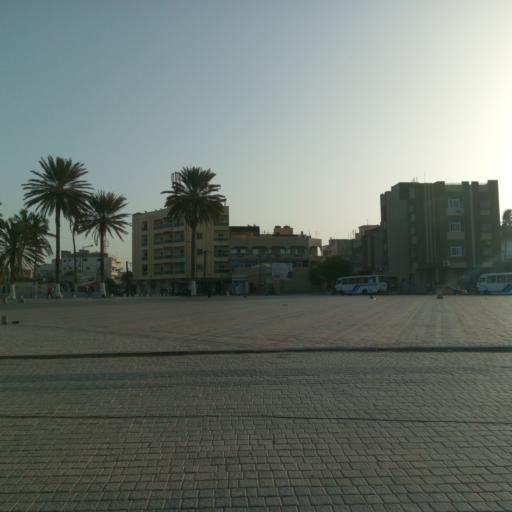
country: SN
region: Dakar
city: Dakar
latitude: 14.6931
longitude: -17.4481
